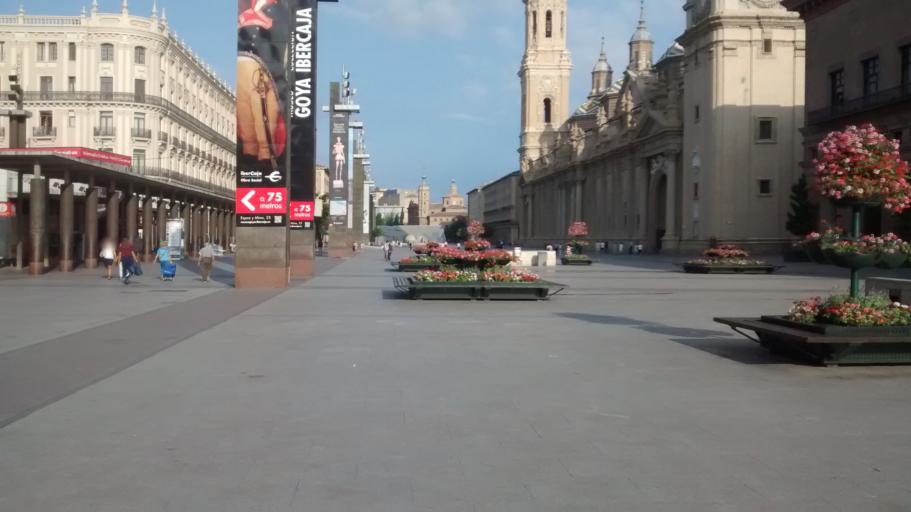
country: ES
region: Aragon
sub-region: Provincia de Zaragoza
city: Zaragoza
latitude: 41.6556
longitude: -0.8774
